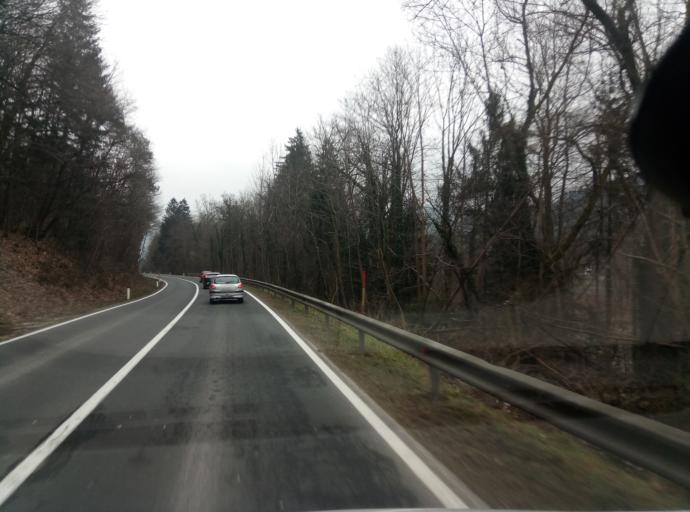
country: SI
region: Moravce
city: Moravce
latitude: 46.0904
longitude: 14.7022
